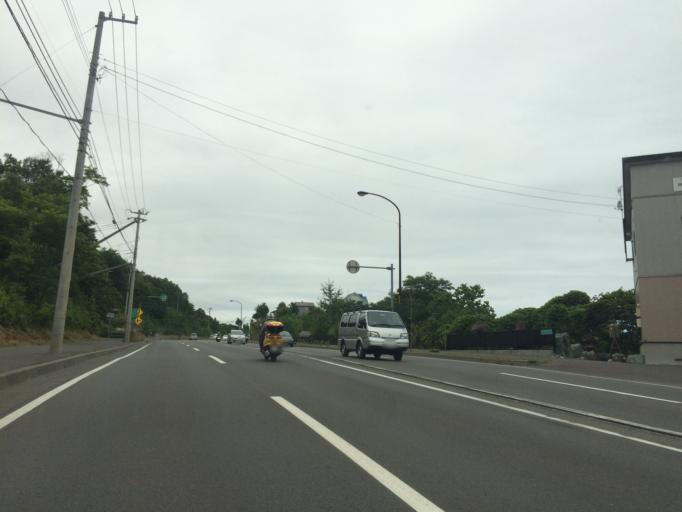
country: JP
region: Hokkaido
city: Otaru
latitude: 43.1458
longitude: 141.1406
